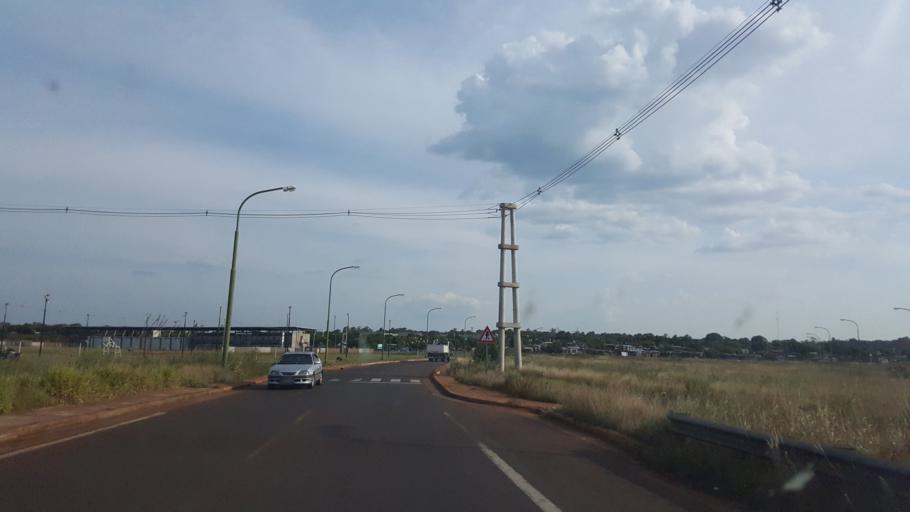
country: AR
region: Misiones
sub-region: Departamento de Capital
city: Posadas
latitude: -27.4158
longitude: -55.8873
